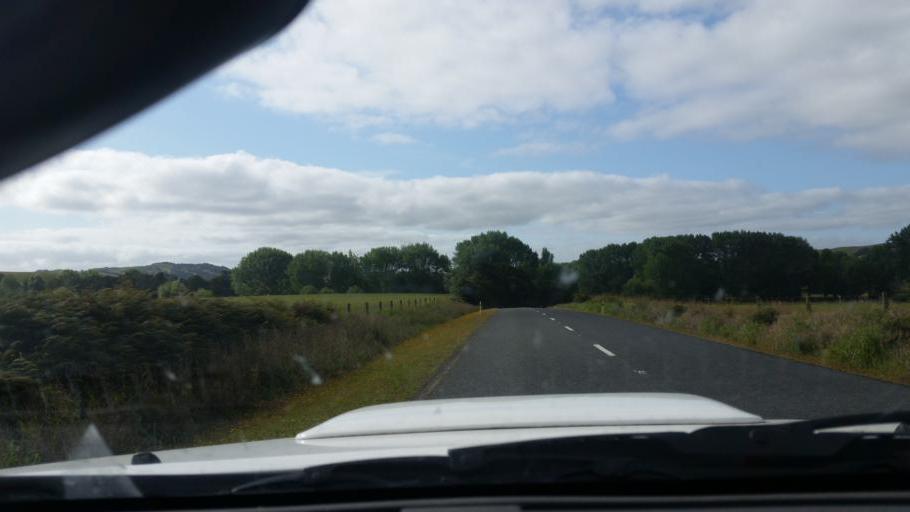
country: NZ
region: Northland
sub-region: Kaipara District
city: Dargaville
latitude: -35.8378
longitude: 173.8440
